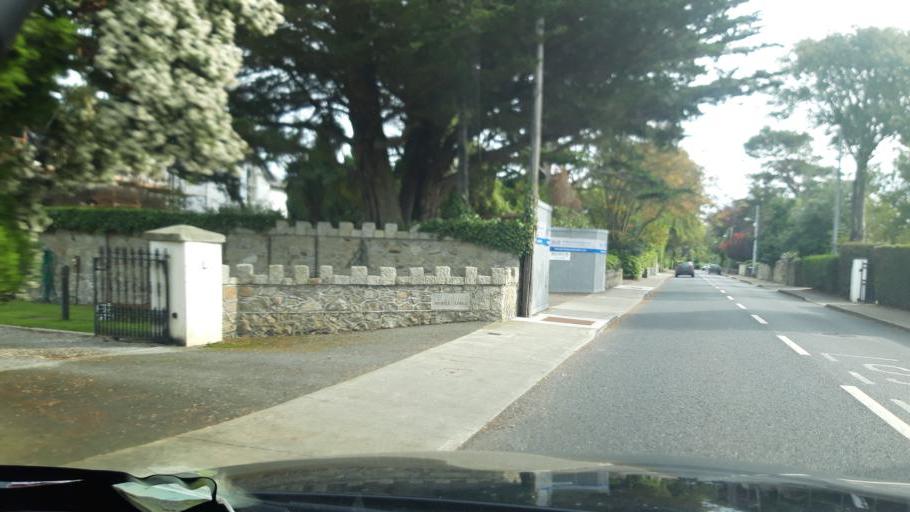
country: IE
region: Leinster
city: Foxrock
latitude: 53.2725
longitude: -6.1884
